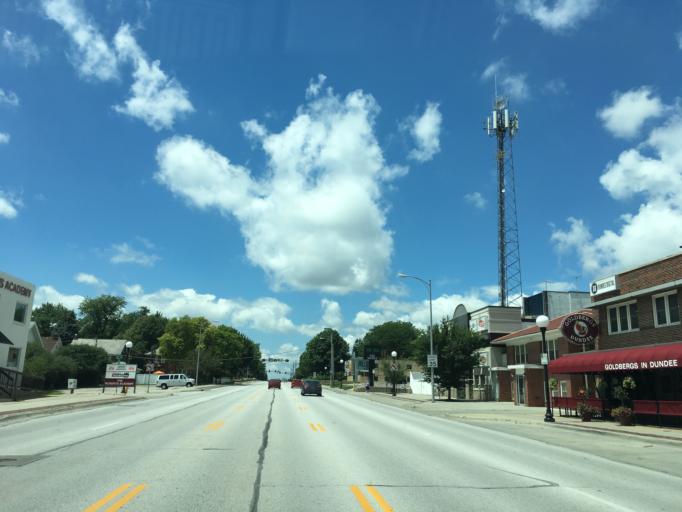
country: US
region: Nebraska
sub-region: Douglas County
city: Omaha
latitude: 41.2596
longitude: -95.9905
